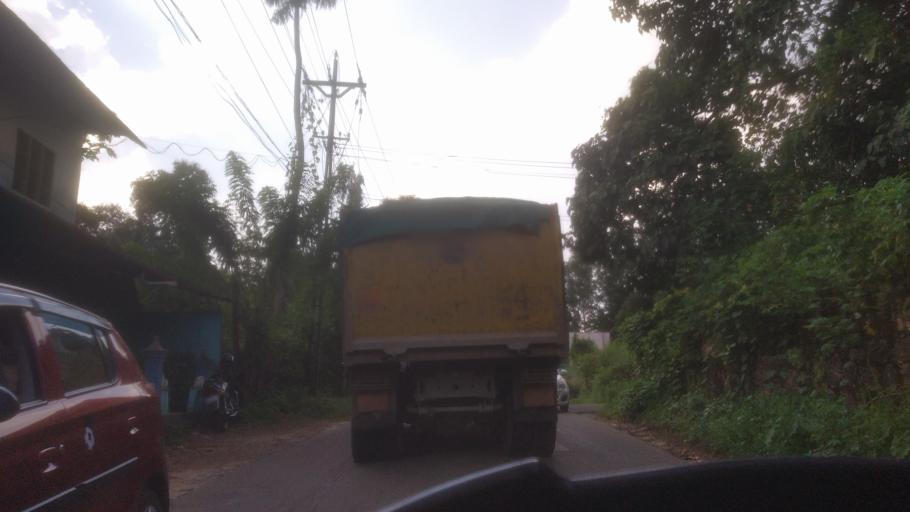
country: IN
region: Kerala
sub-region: Ernakulam
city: Kotamangalam
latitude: 10.0049
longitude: 76.6843
